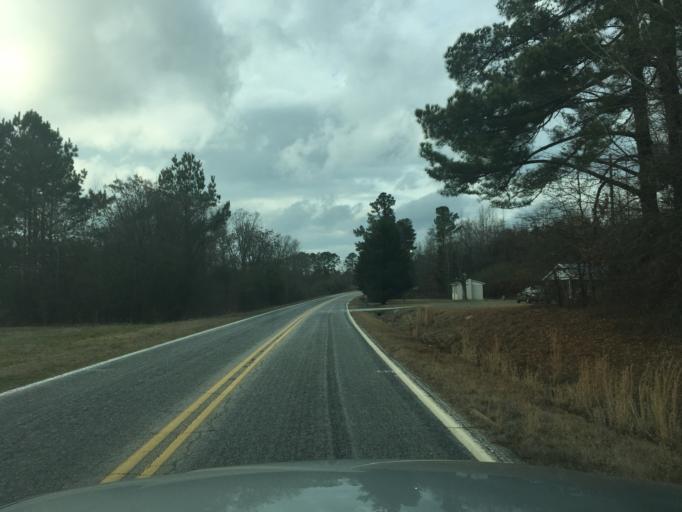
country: US
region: South Carolina
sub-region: Abbeville County
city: Abbeville
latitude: 34.2439
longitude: -82.4096
